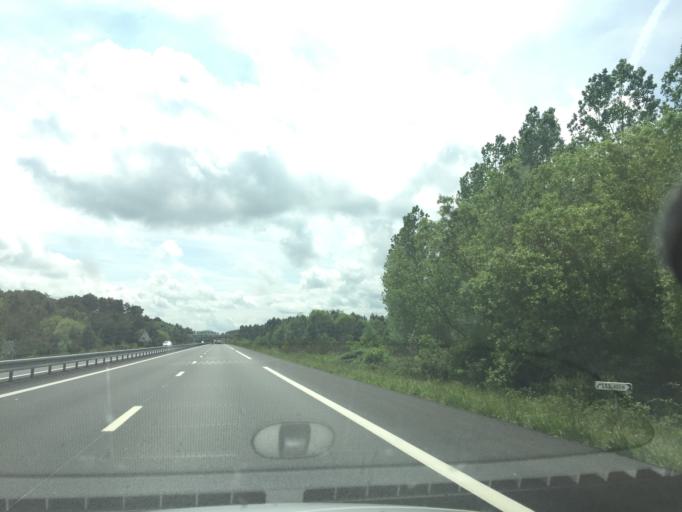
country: FR
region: Pays de la Loire
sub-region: Departement de la Sarthe
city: Brette-les-Pins
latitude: 47.9287
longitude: 0.3061
